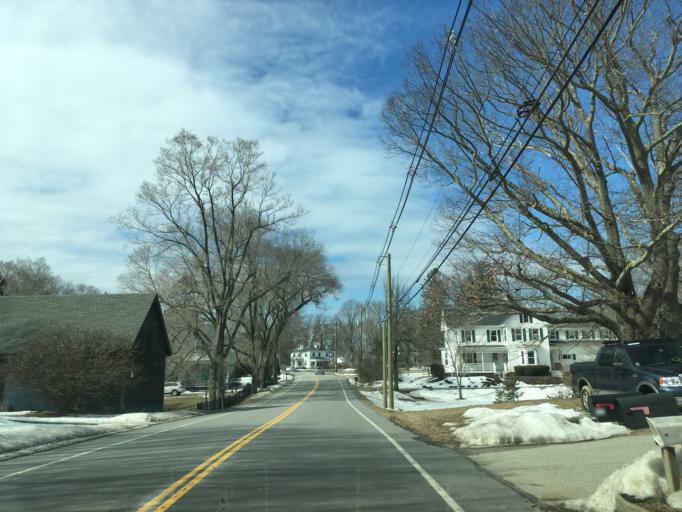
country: US
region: New Hampshire
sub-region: Rockingham County
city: North Hampton
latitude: 42.9775
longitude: -70.8424
